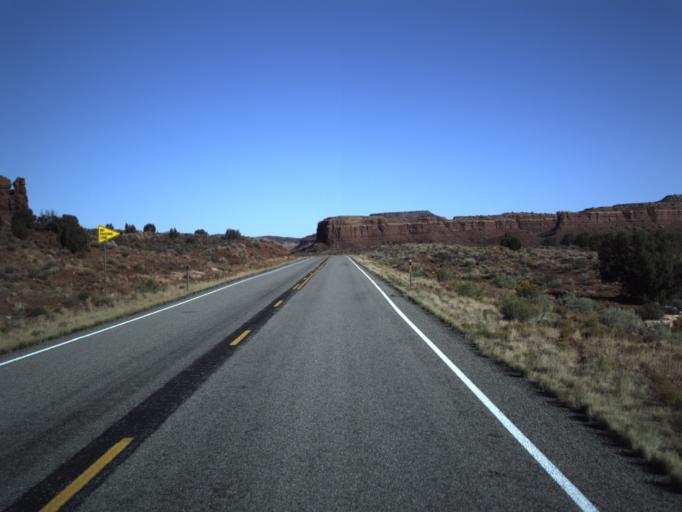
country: US
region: Utah
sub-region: San Juan County
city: Blanding
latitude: 37.6960
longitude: -110.2306
